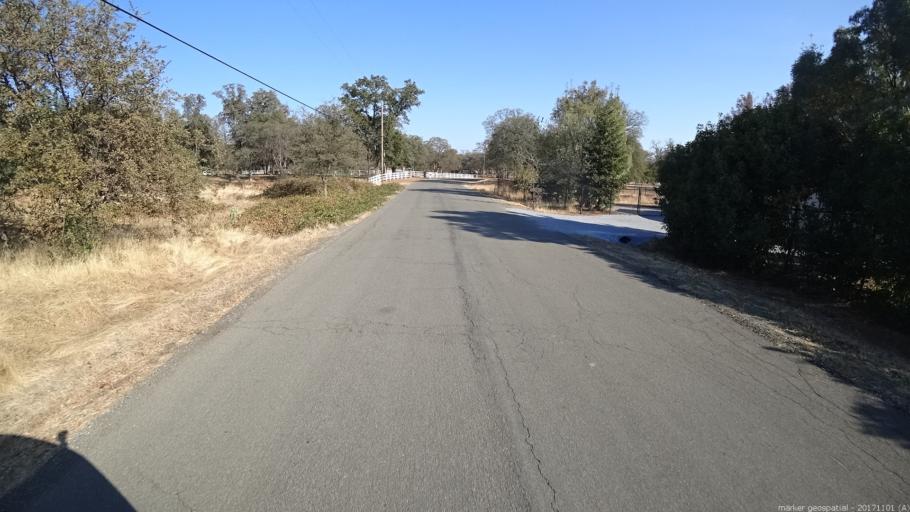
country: US
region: California
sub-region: Shasta County
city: Shasta Lake
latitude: 40.6789
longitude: -122.3366
